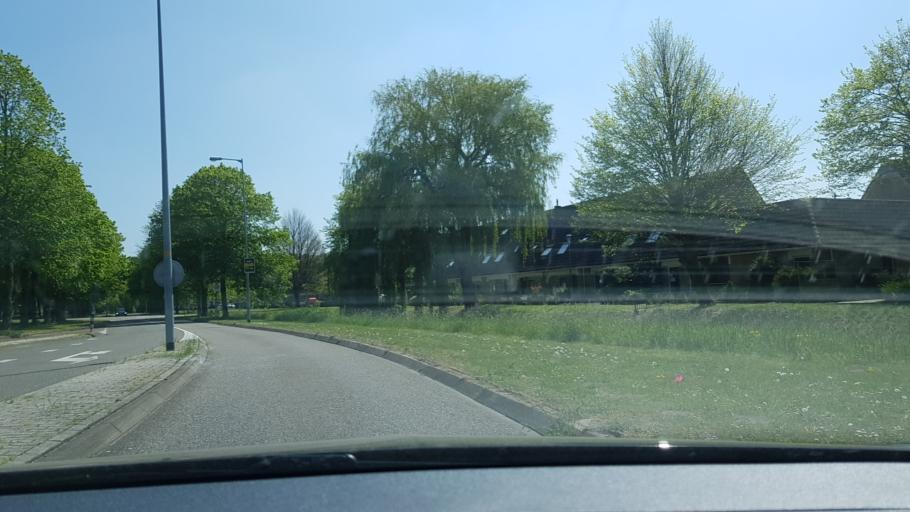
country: NL
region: North Holland
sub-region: Gemeente Haarlemmermeer
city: Hoofddorp
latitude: 52.3195
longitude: 4.6618
